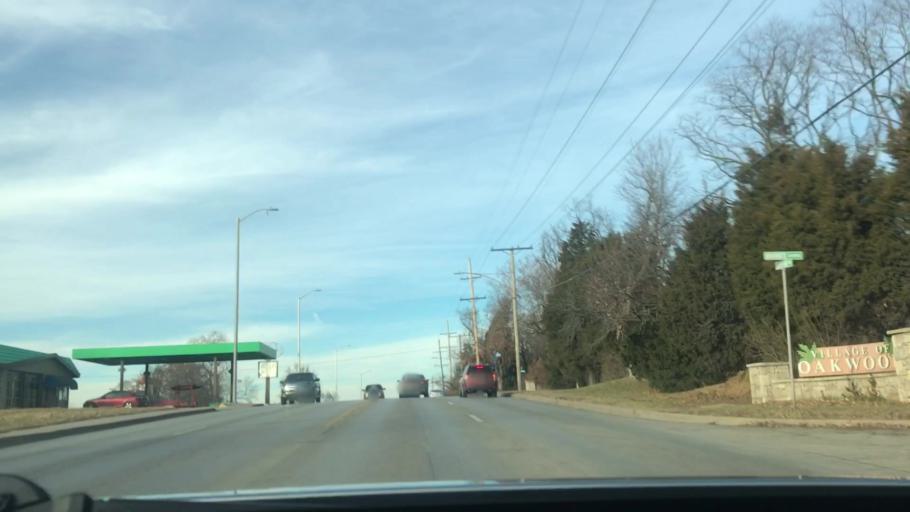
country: US
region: Missouri
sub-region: Clay County
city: Gladstone
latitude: 39.1984
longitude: -94.5764
